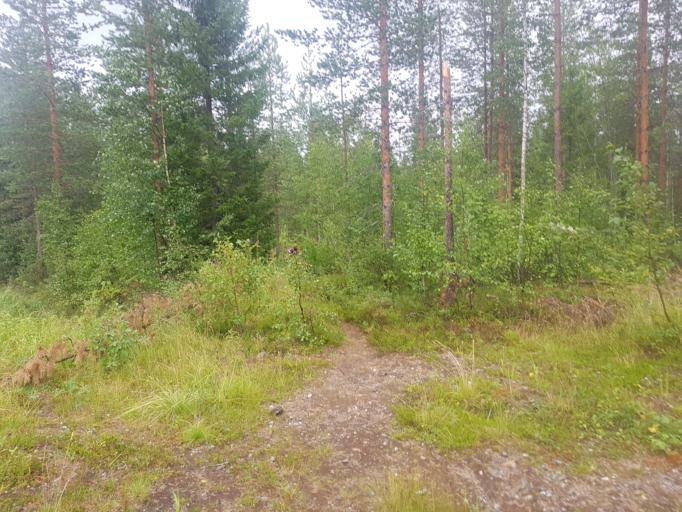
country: FI
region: Kainuu
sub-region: Kehys-Kainuu
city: Kuhmo
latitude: 64.4544
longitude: 29.6575
